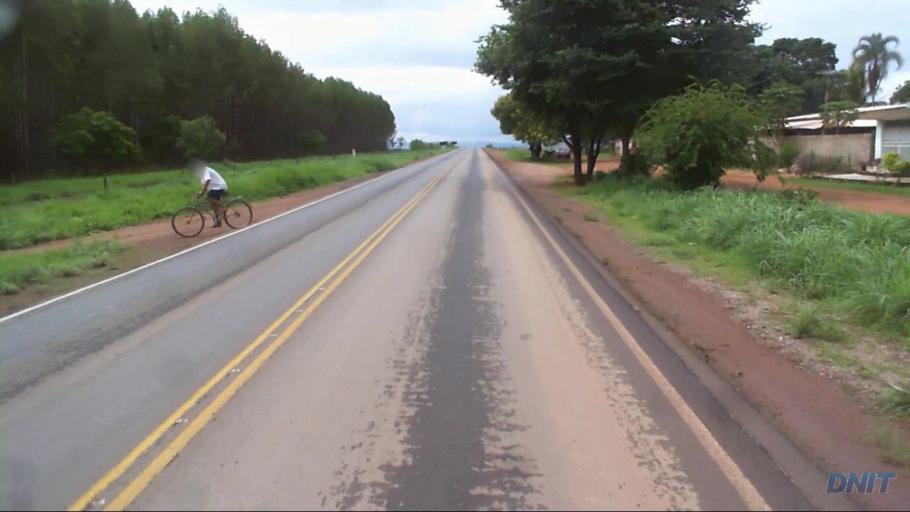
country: BR
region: Goias
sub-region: Padre Bernardo
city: Padre Bernardo
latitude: -15.2664
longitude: -48.2639
